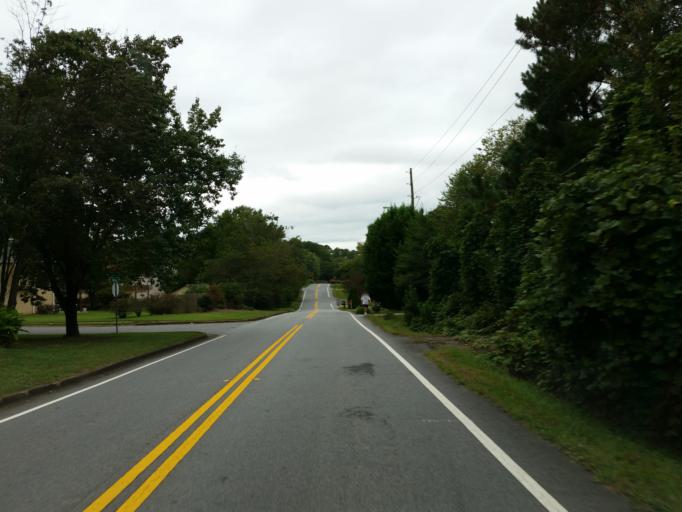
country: US
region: Georgia
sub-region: Cobb County
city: Marietta
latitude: 34.0098
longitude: -84.5131
